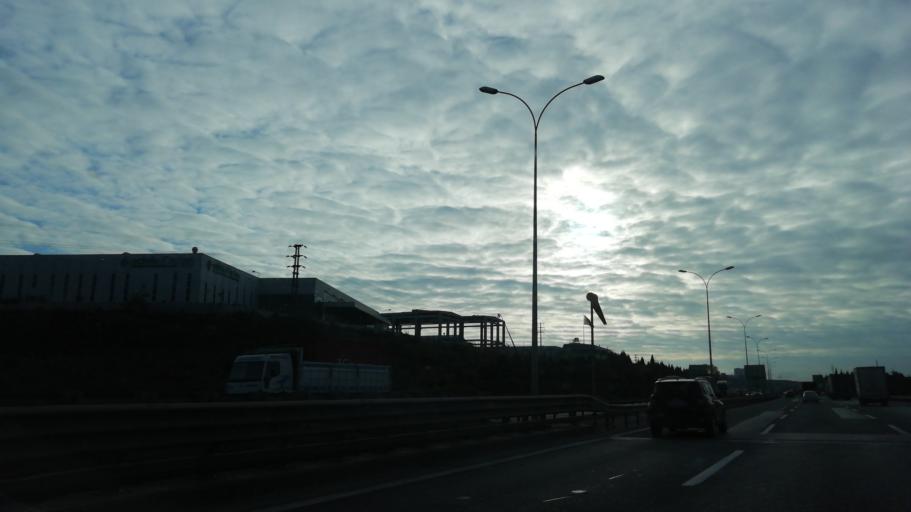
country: TR
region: Kocaeli
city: Balcik
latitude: 40.8644
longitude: 29.4001
